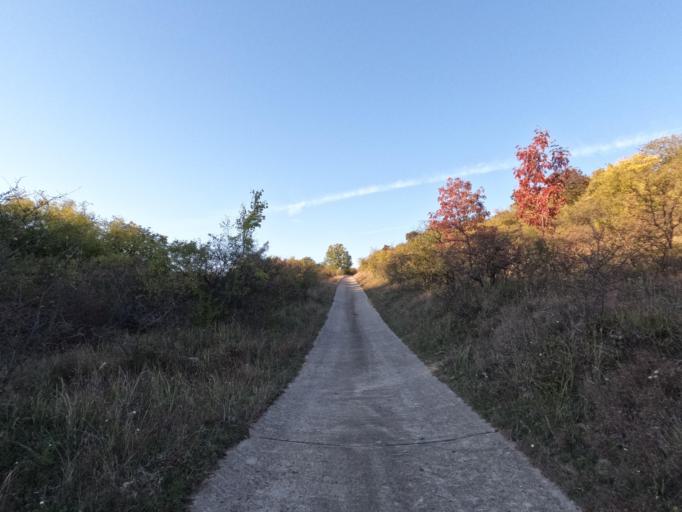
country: HU
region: Tolna
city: Szekszard
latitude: 46.3056
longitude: 18.6609
